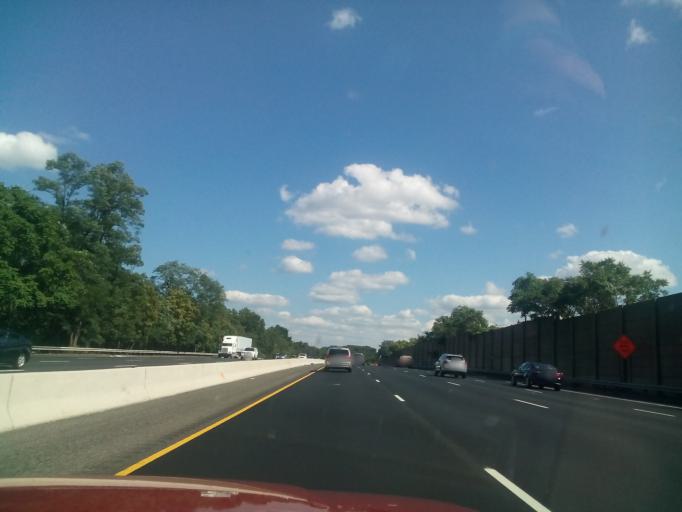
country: US
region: New Jersey
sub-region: Morris County
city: Rockaway
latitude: 40.8906
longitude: -74.4801
